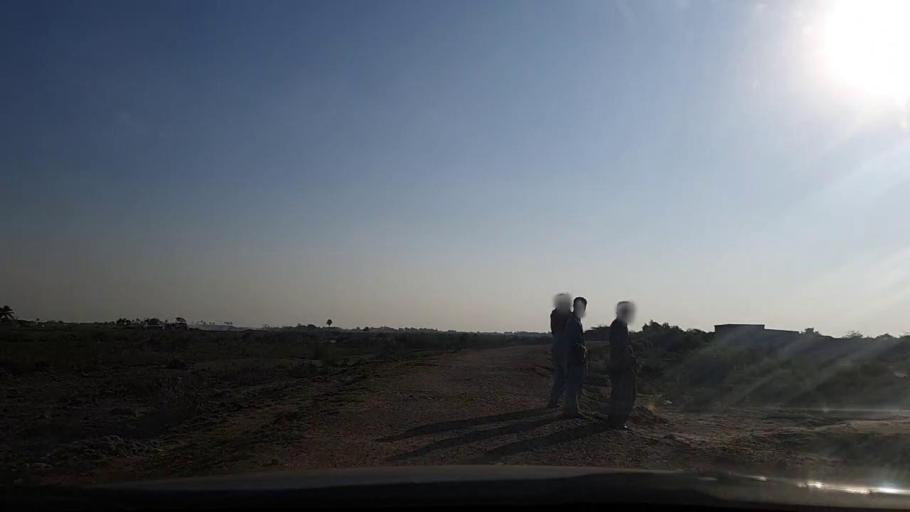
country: PK
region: Sindh
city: Mirpur Sakro
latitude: 24.5139
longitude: 67.6323
